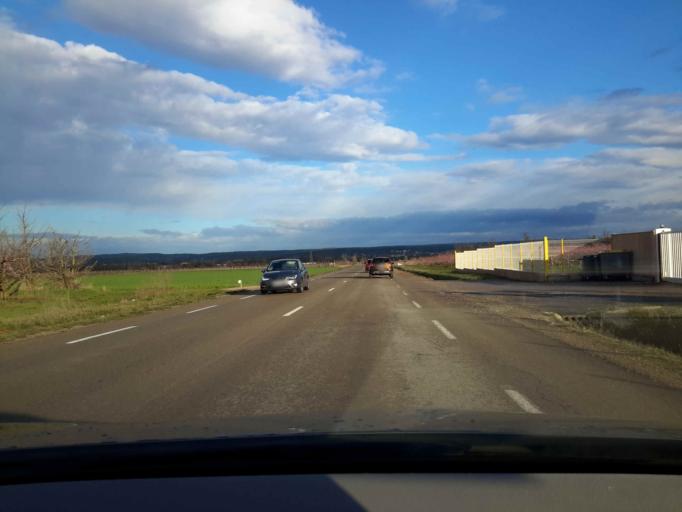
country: FR
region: Languedoc-Roussillon
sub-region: Departement du Gard
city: Aubord
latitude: 43.7601
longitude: 4.3365
